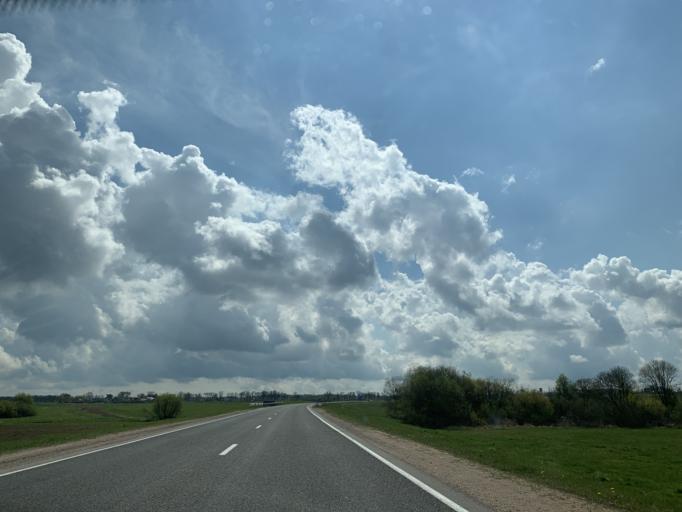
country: BY
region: Minsk
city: Nyasvizh
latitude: 53.2356
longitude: 26.7178
